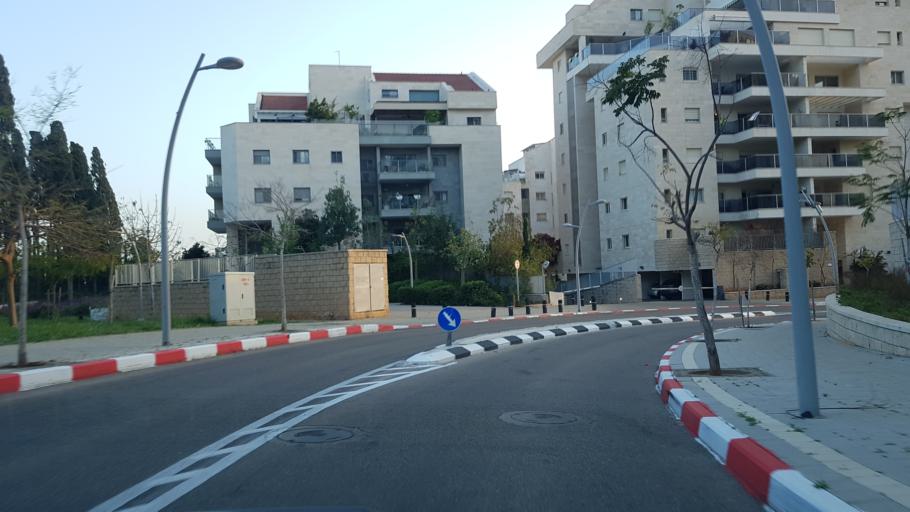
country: IL
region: Central District
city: Kfar Saba
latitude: 32.1953
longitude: 34.8971
